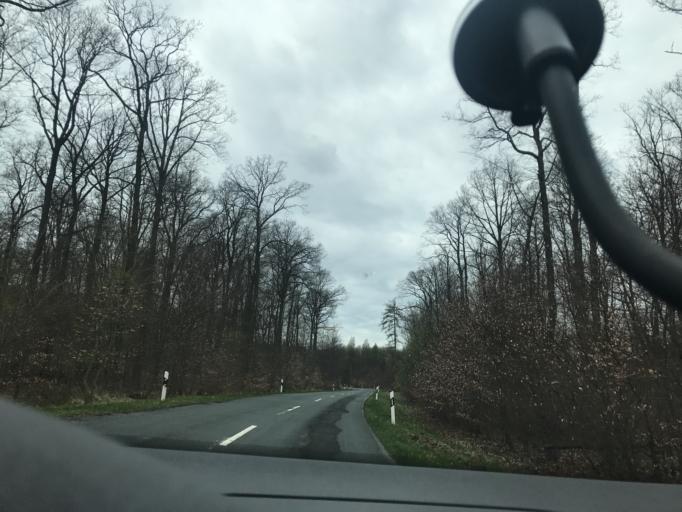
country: DE
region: Lower Saxony
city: Warberg
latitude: 52.1643
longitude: 10.8944
